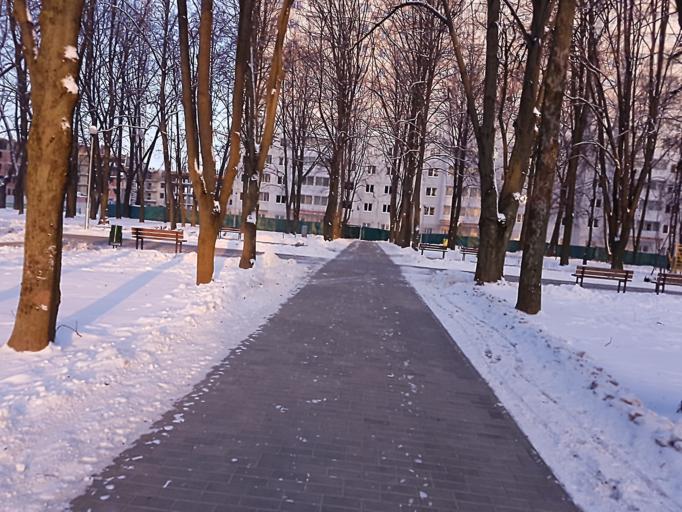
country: BY
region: Minsk
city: Minsk
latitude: 53.8860
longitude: 27.5194
